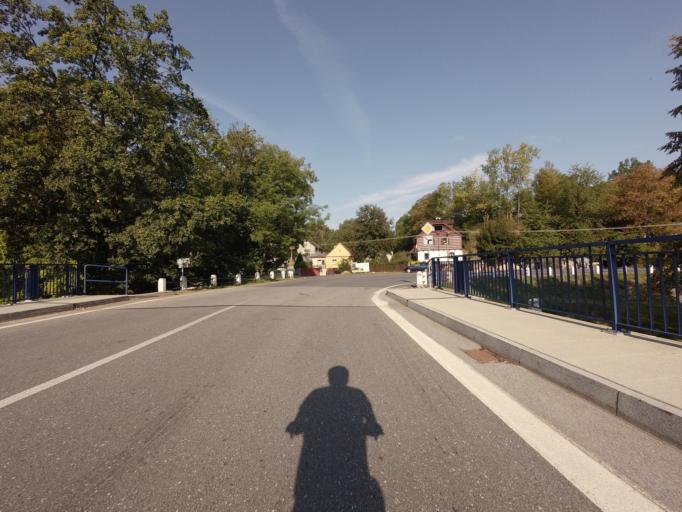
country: CZ
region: Jihocesky
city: Tyn nad Vltavou
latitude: 49.2529
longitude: 14.4199
